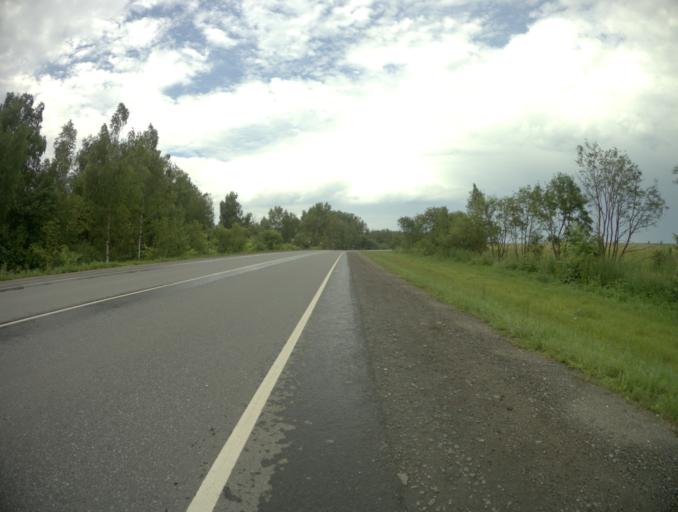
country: RU
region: Vladimir
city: Bogolyubovo
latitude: 56.2115
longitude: 40.4407
